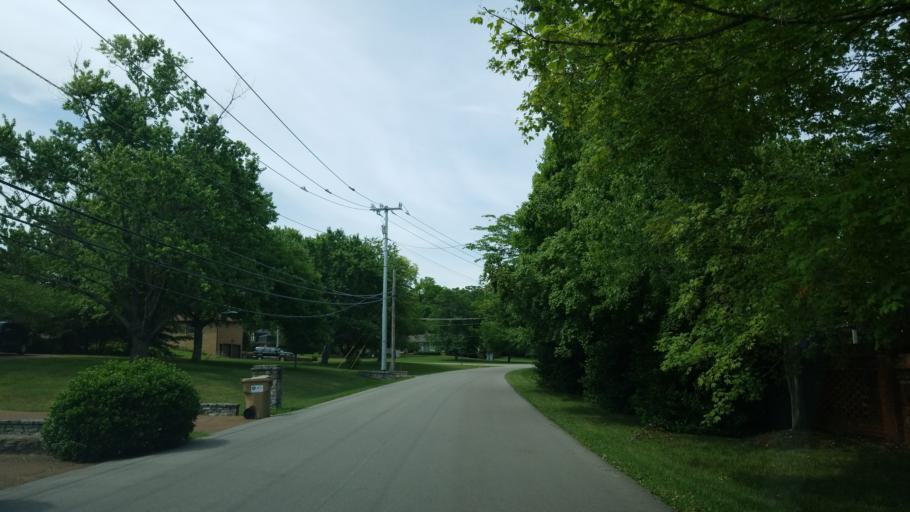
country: US
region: Tennessee
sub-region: Davidson County
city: Forest Hills
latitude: 36.0370
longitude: -86.8216
